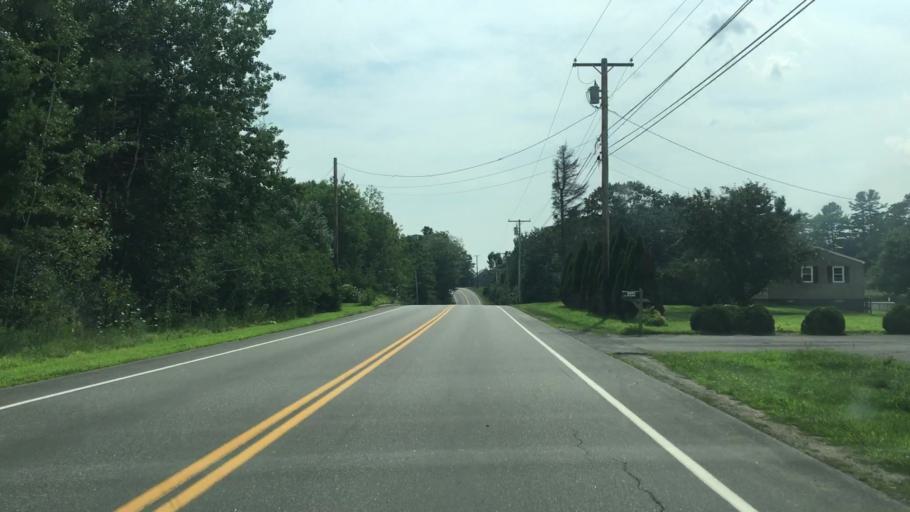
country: US
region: Maine
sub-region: Kennebec County
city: Windsor
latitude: 44.2903
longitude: -69.5884
